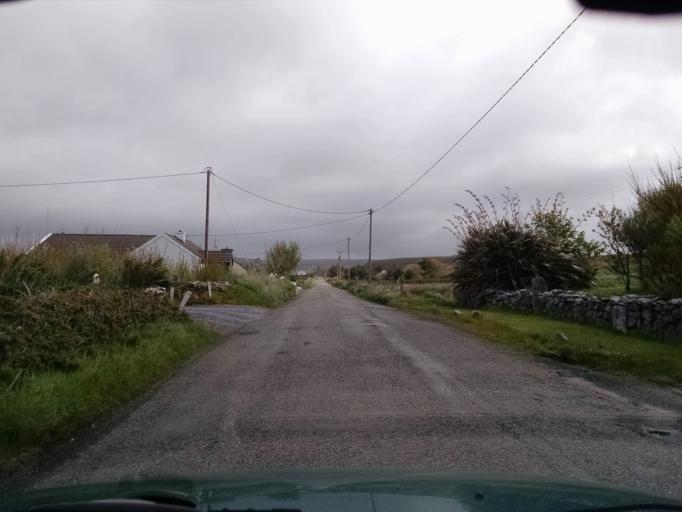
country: IE
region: Connaught
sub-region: County Galway
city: Bearna
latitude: 53.0373
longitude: -9.3545
